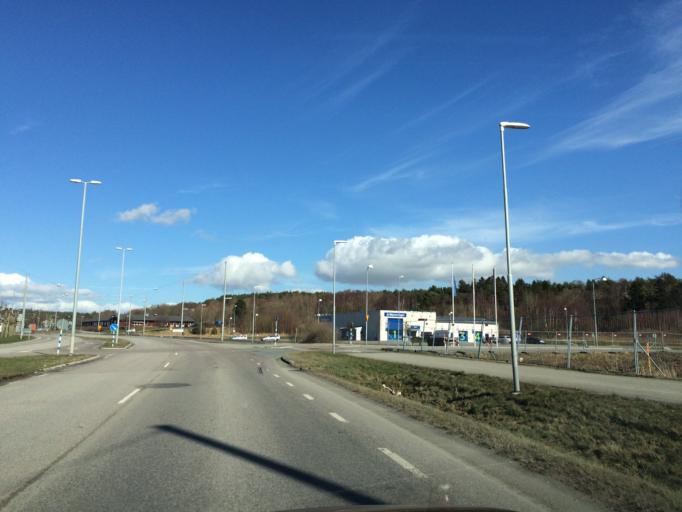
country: SE
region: Vaestra Goetaland
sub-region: Goteborg
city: Majorna
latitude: 57.7153
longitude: 11.8469
